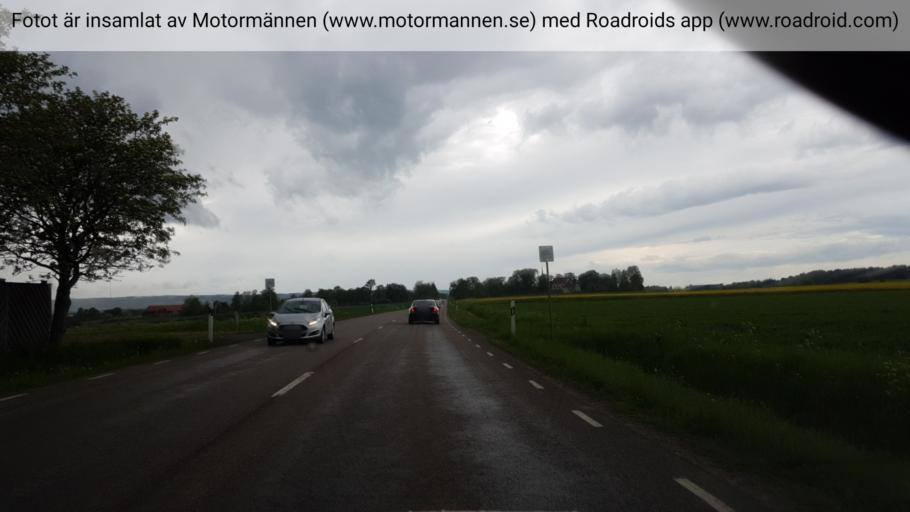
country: SE
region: Vaestra Goetaland
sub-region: Skovde Kommun
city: Skoevde
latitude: 58.3848
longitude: 13.9440
